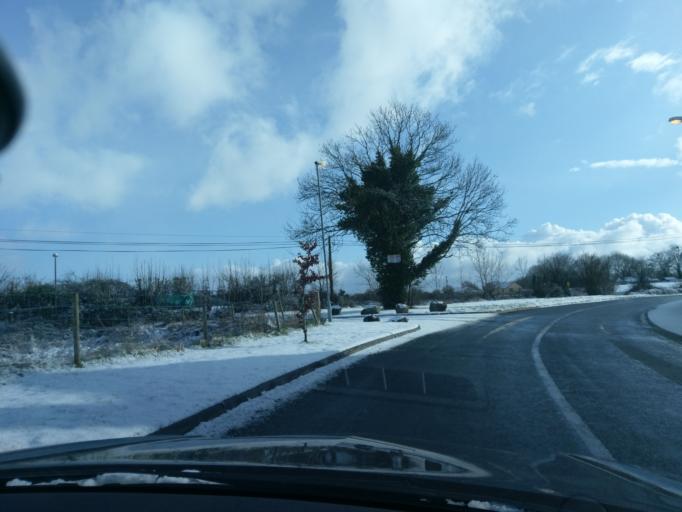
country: IE
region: Connaught
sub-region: County Galway
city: Athenry
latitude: 53.2265
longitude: -8.7376
